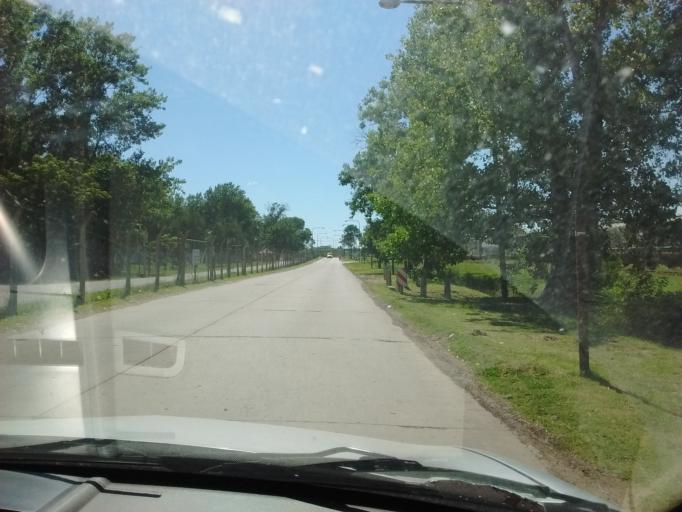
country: AR
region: Santa Fe
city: Funes
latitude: -32.9213
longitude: -60.7837
